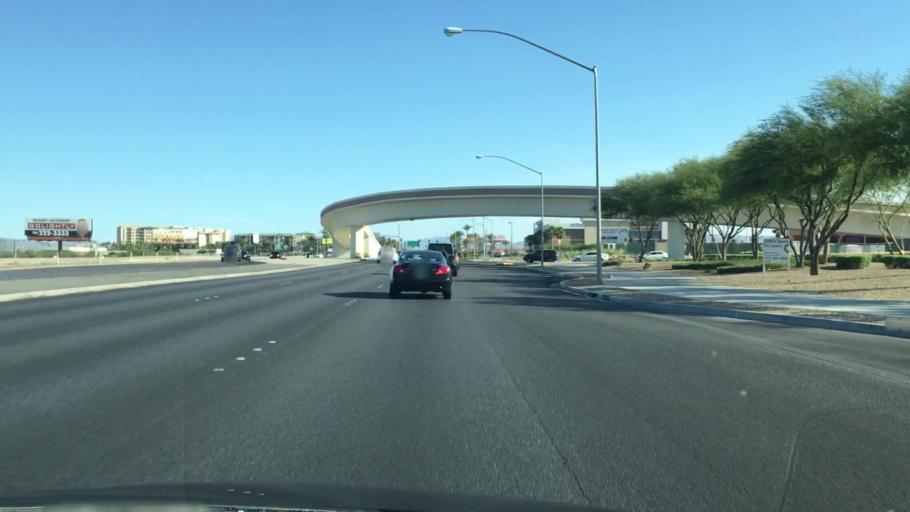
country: US
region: Nevada
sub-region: Clark County
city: Paradise
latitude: 36.0675
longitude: -115.1726
